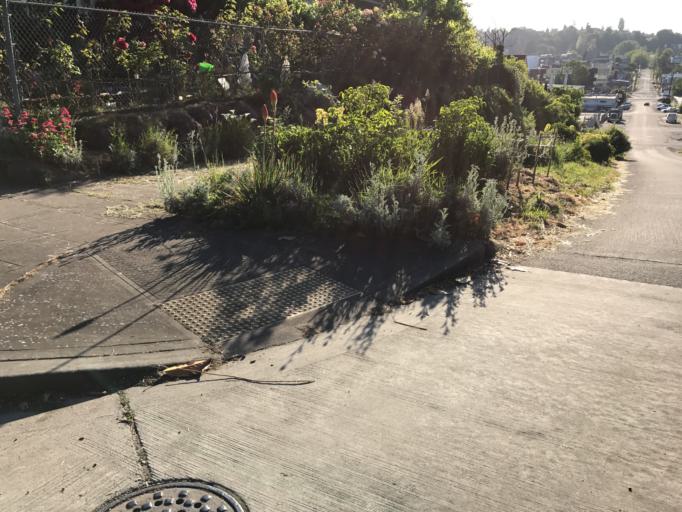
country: US
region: Washington
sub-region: King County
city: Seattle
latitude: 47.5855
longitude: -122.3081
